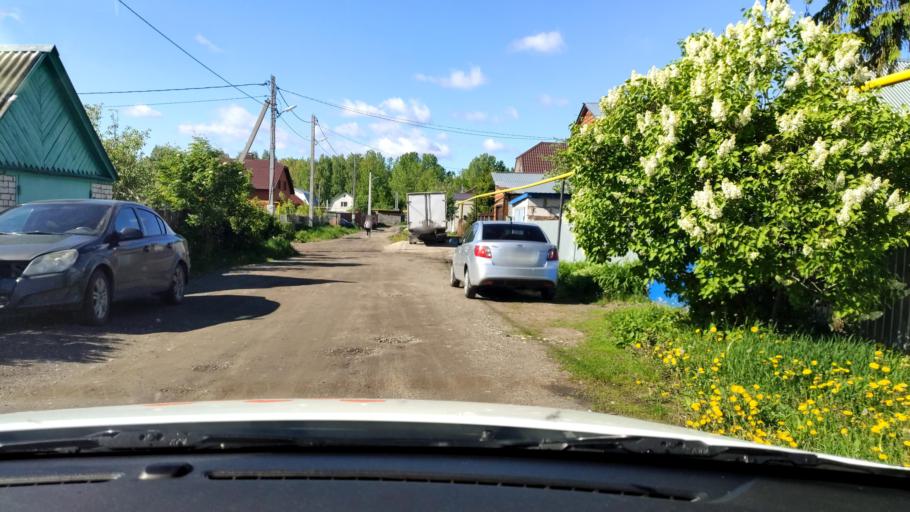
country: RU
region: Tatarstan
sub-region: Gorod Kazan'
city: Kazan
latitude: 55.7362
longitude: 49.0904
